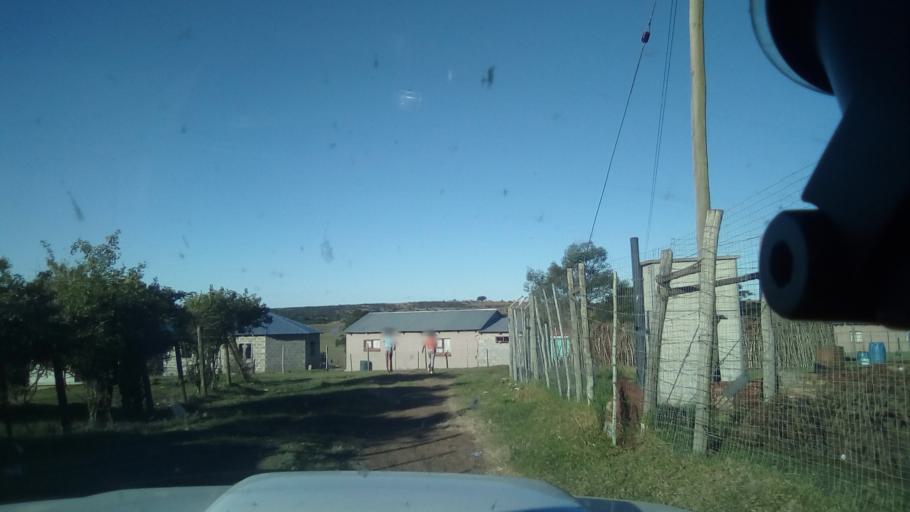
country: ZA
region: Eastern Cape
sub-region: Buffalo City Metropolitan Municipality
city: Bhisho
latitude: -32.9505
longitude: 27.2946
